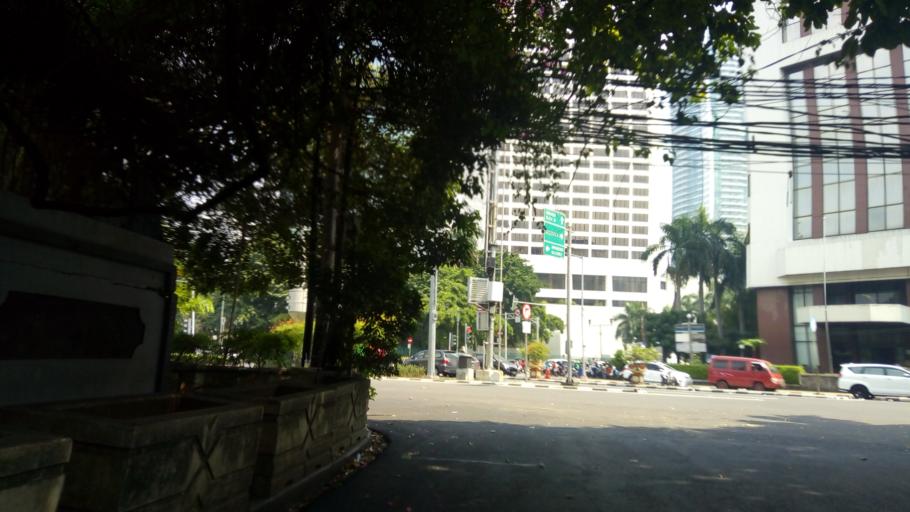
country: ID
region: Jakarta Raya
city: Jakarta
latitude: -6.1965
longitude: 106.8253
